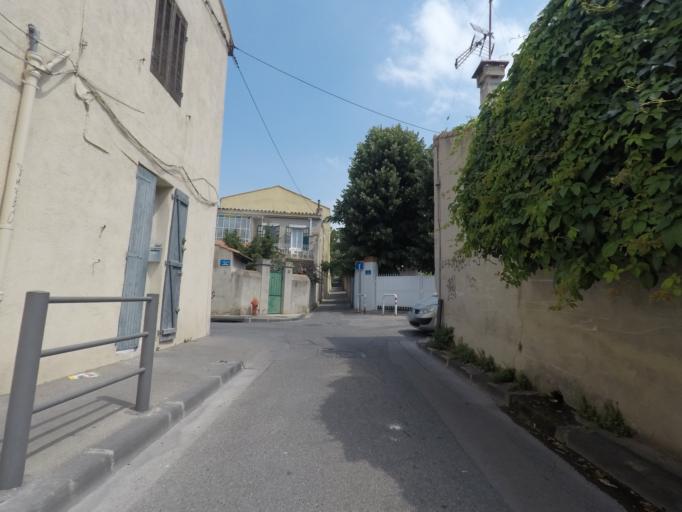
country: FR
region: Provence-Alpes-Cote d'Azur
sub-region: Departement des Bouches-du-Rhone
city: Marseille 10
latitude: 43.2812
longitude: 5.4092
